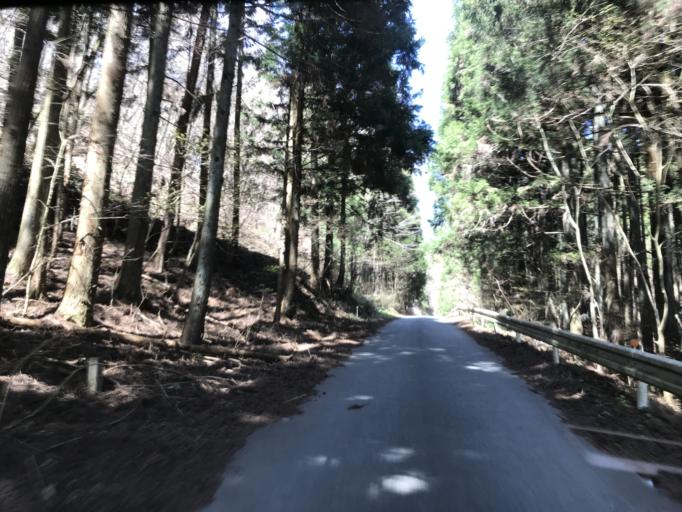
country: JP
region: Iwate
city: Ichinoseki
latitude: 38.8166
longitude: 141.2809
